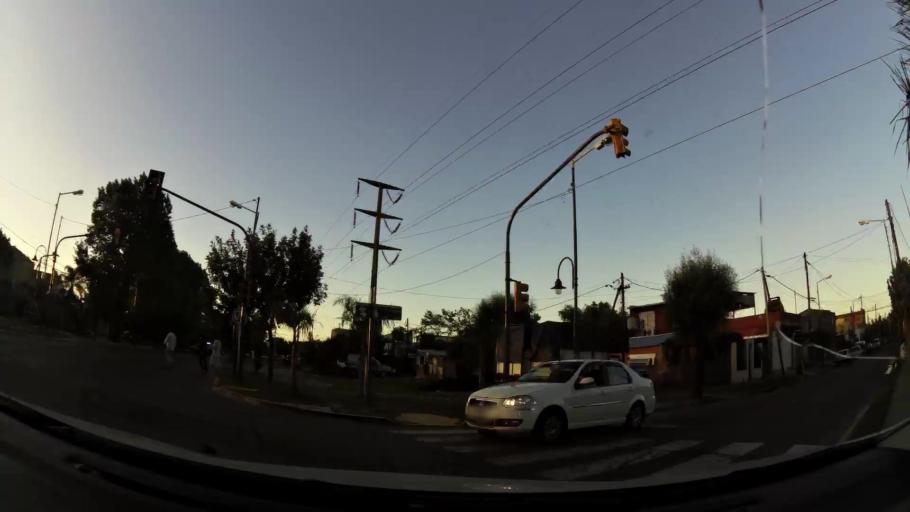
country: AR
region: Buenos Aires
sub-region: Partido de Tigre
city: Tigre
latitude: -34.4455
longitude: -58.5748
